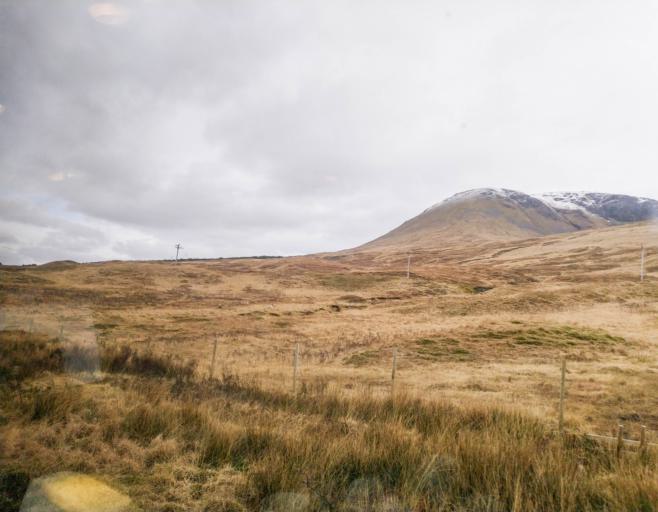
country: GB
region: Scotland
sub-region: Highland
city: Spean Bridge
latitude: 56.5113
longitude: -4.7607
